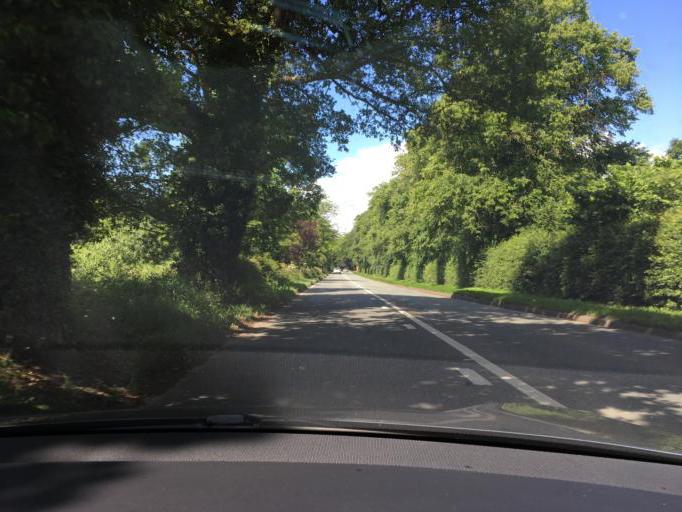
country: GB
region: England
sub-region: Cheshire East
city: Mobberley
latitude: 53.2888
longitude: -2.3397
